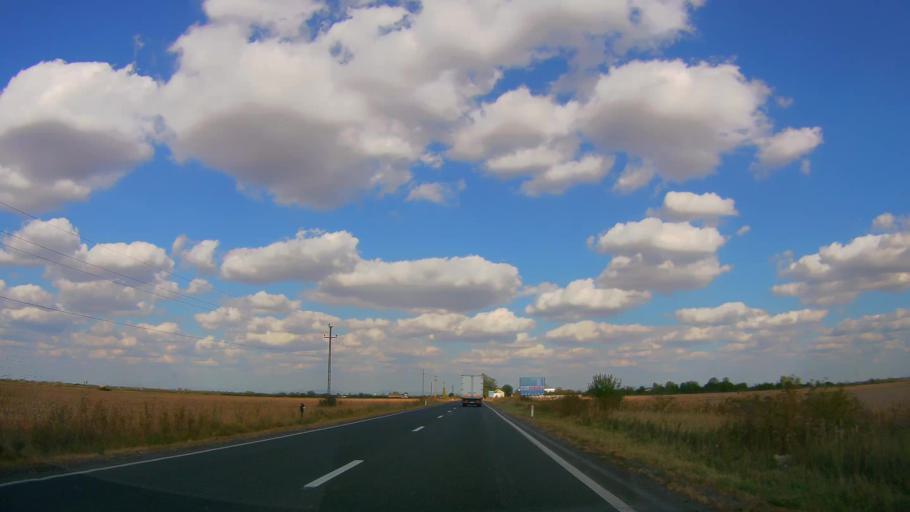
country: RO
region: Satu Mare
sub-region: Oras Ardud
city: Madaras
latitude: 47.7202
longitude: 22.8823
